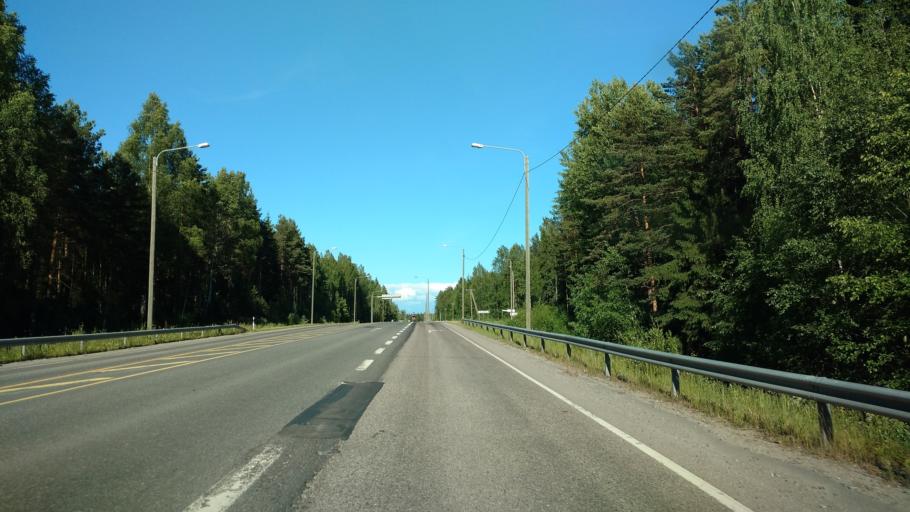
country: FI
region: Varsinais-Suomi
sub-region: Salo
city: Pertteli
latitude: 60.3819
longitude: 23.2197
